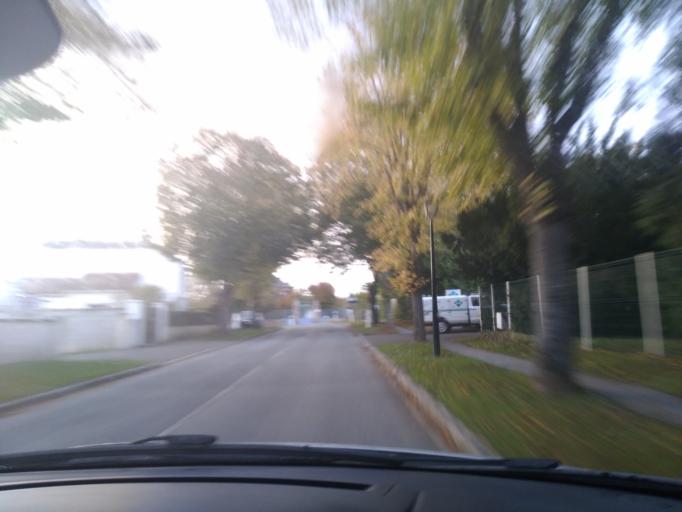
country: FR
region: Ile-de-France
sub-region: Departement des Yvelines
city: Chavenay
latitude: 48.8558
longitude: 1.9790
